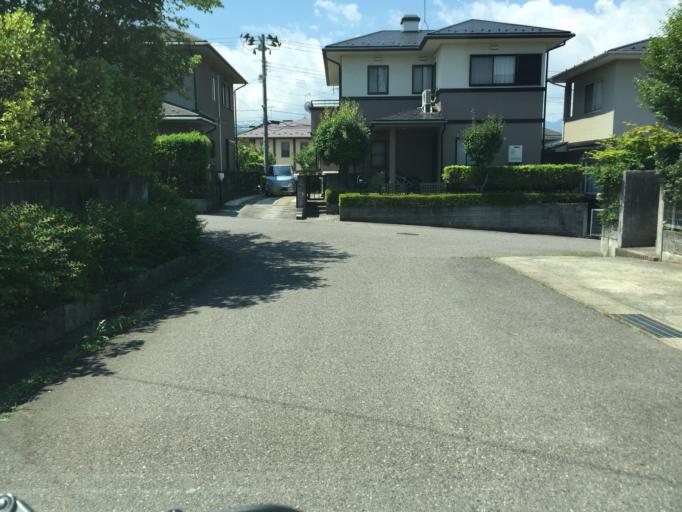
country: JP
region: Fukushima
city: Fukushima-shi
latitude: 37.7218
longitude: 140.4087
